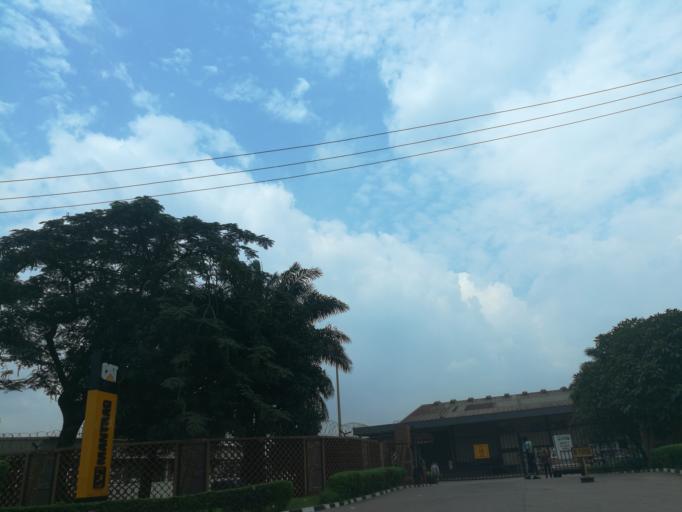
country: NG
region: Lagos
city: Ojota
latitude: 6.6047
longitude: 3.3671
